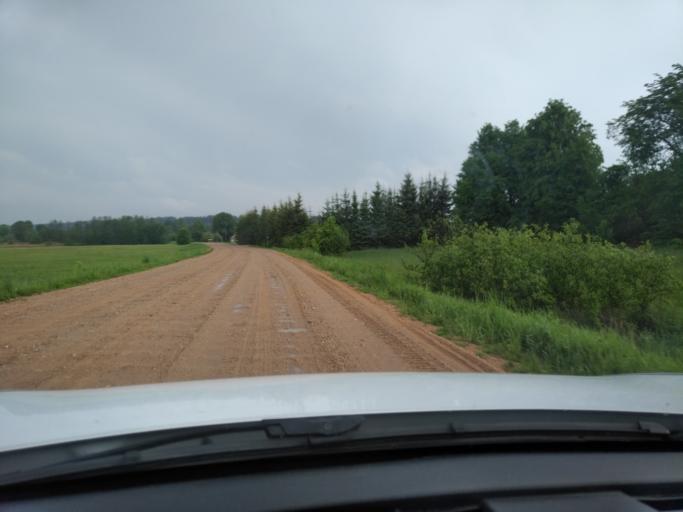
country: LT
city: Ignalina
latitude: 55.2583
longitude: 26.1227
